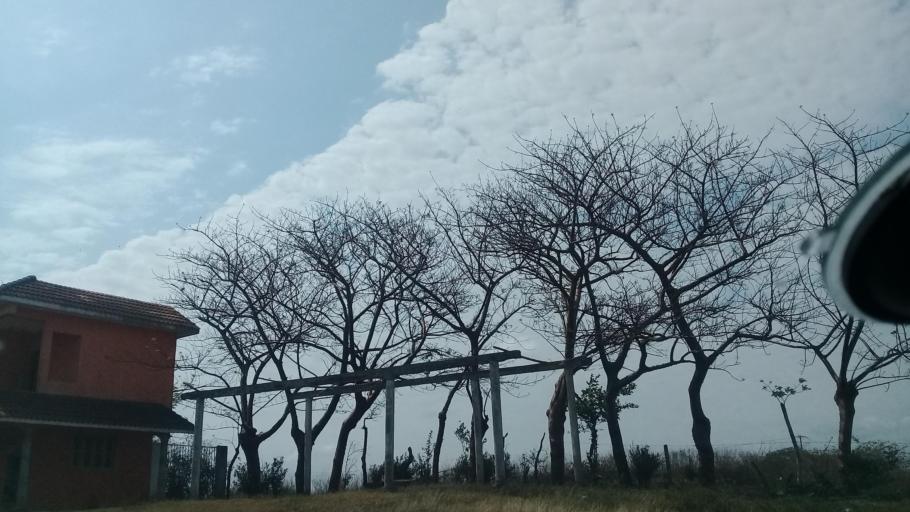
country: MX
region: Veracruz
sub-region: Veracruz
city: Delfino Victoria (Santa Fe)
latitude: 19.2128
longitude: -96.3179
